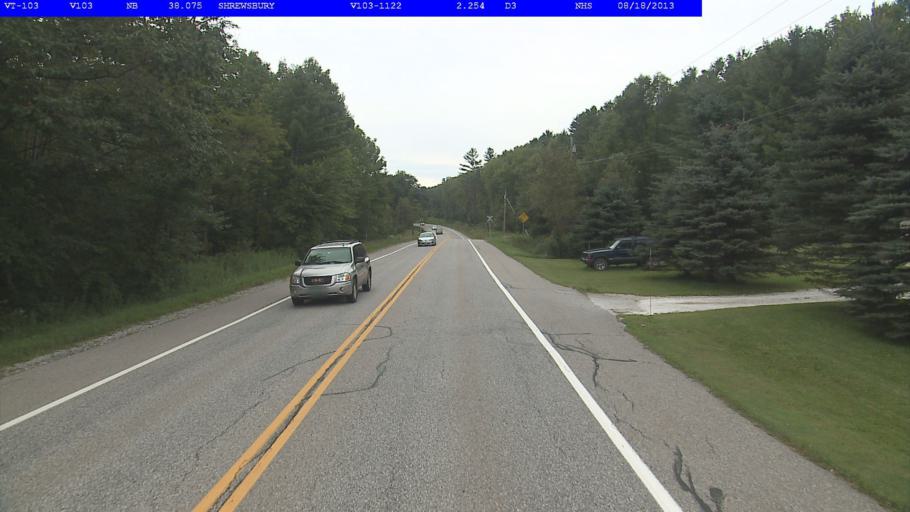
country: US
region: Vermont
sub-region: Rutland County
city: Rutland
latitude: 43.5049
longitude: -72.9022
